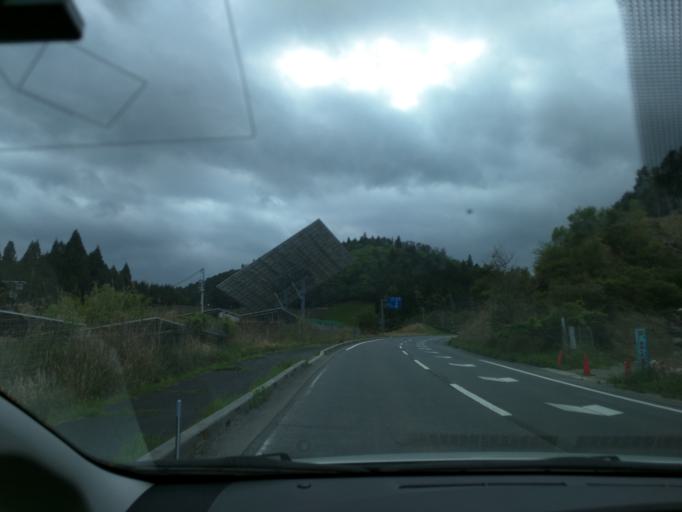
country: JP
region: Shiga Prefecture
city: Kusatsu
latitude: 34.8555
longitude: 135.9622
